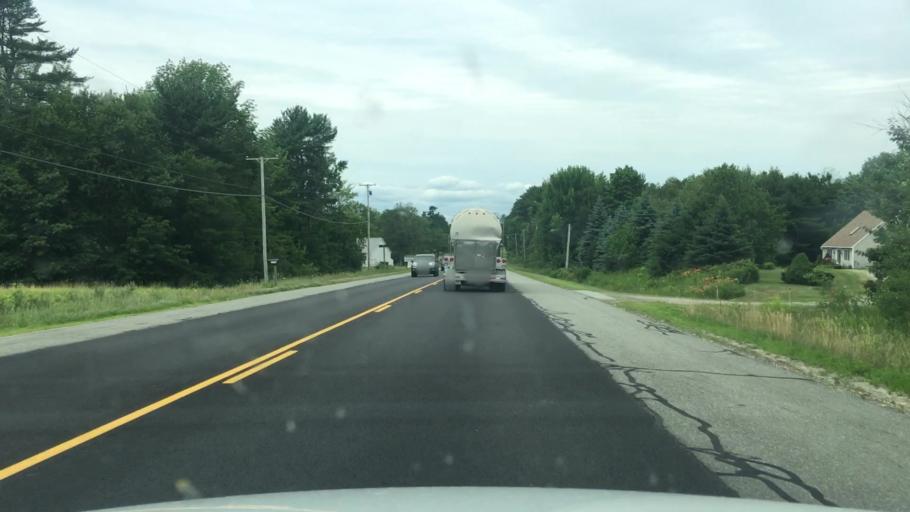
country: US
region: Maine
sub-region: Waldo County
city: Palermo
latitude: 44.3776
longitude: -69.4498
